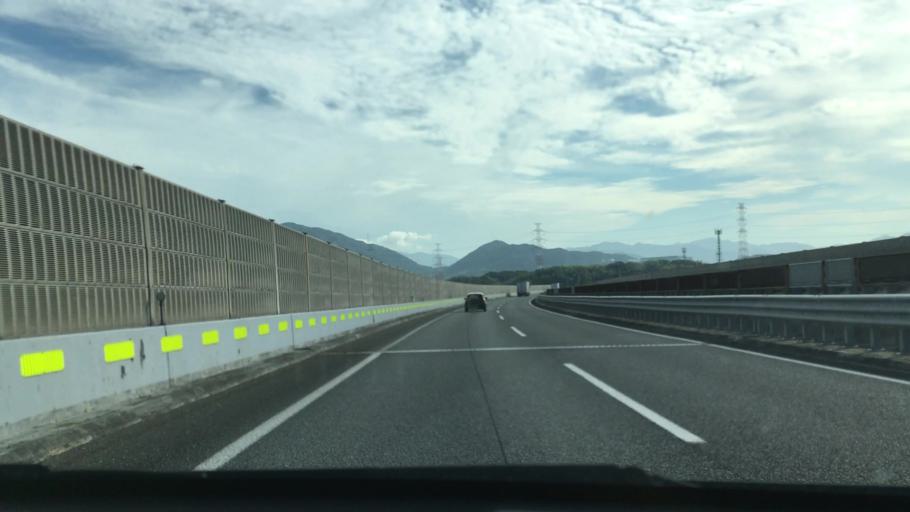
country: JP
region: Fukuoka
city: Kanda
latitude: 33.8364
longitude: 130.9231
